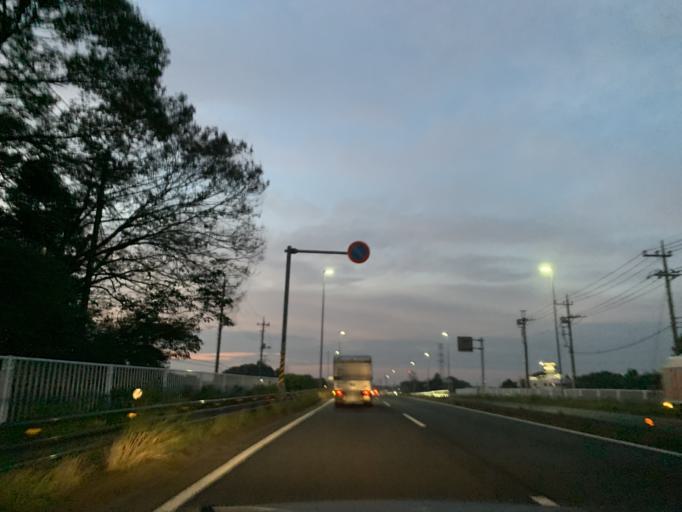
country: JP
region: Chiba
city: Nagareyama
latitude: 35.9158
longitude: 139.9280
